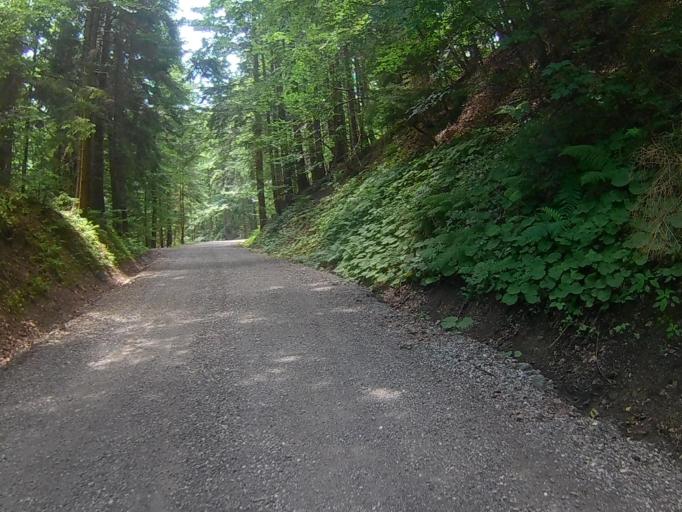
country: SI
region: Maribor
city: Pekre
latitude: 46.5000
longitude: 15.5649
